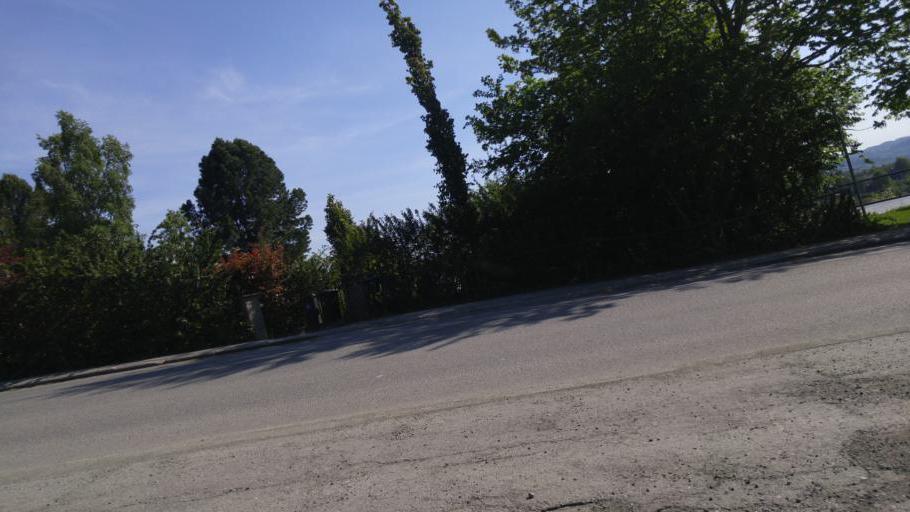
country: NO
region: Sor-Trondelag
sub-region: Trondheim
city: Trondheim
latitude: 63.4168
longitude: 10.4190
